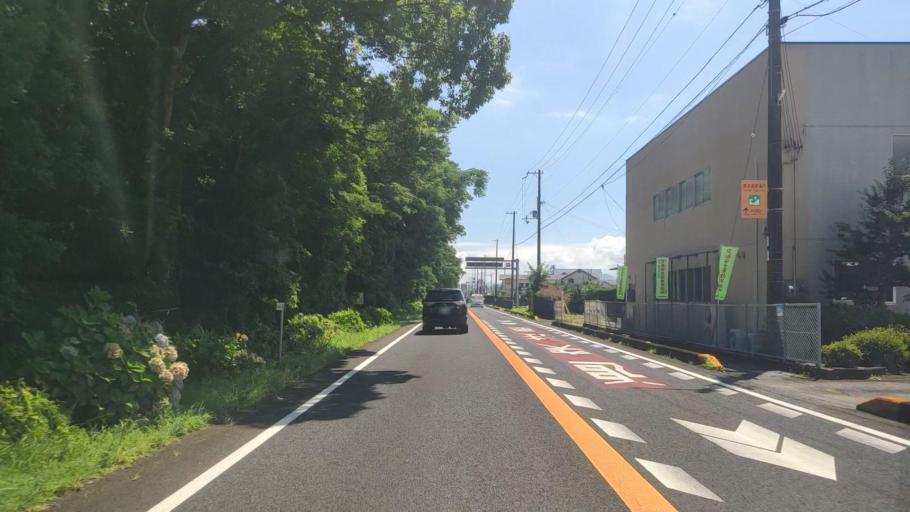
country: JP
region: Wakayama
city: Shingu
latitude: 33.8693
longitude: 136.0832
